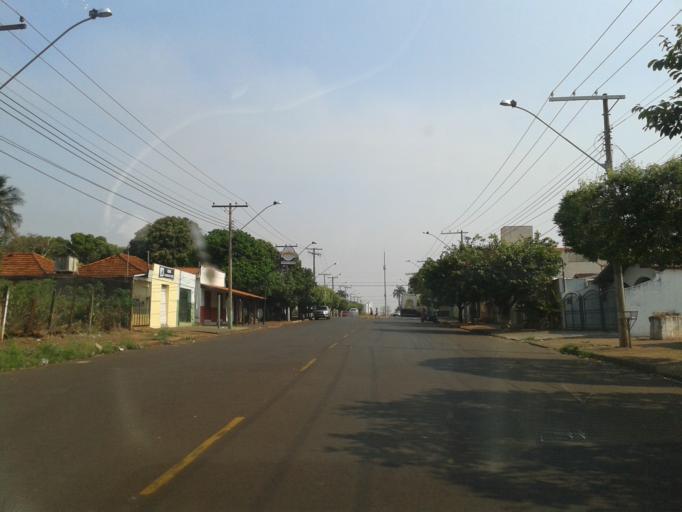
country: BR
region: Minas Gerais
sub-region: Ituiutaba
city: Ituiutaba
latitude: -18.9650
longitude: -49.4493
